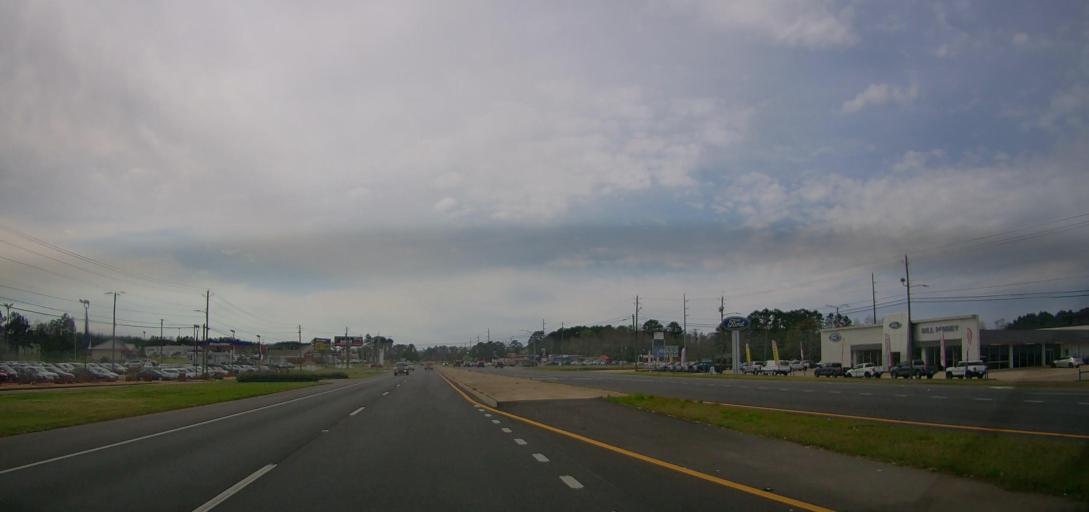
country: US
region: Alabama
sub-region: Walker County
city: Jasper
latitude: 33.8377
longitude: -87.2284
